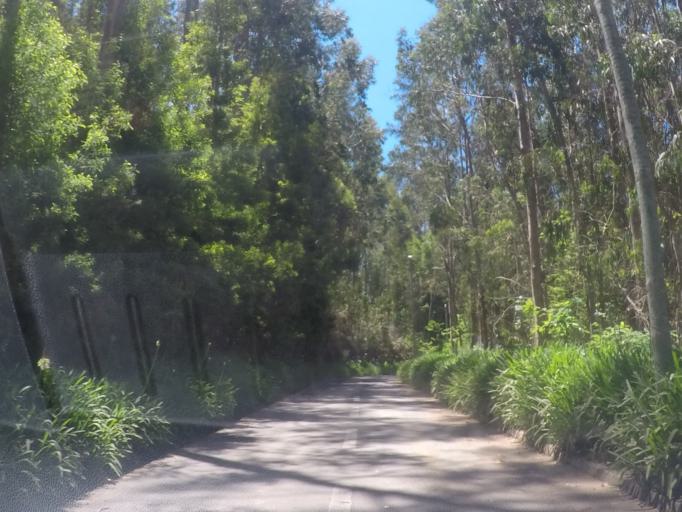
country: PT
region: Madeira
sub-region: Camara de Lobos
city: Curral das Freiras
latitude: 32.6953
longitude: -16.9780
